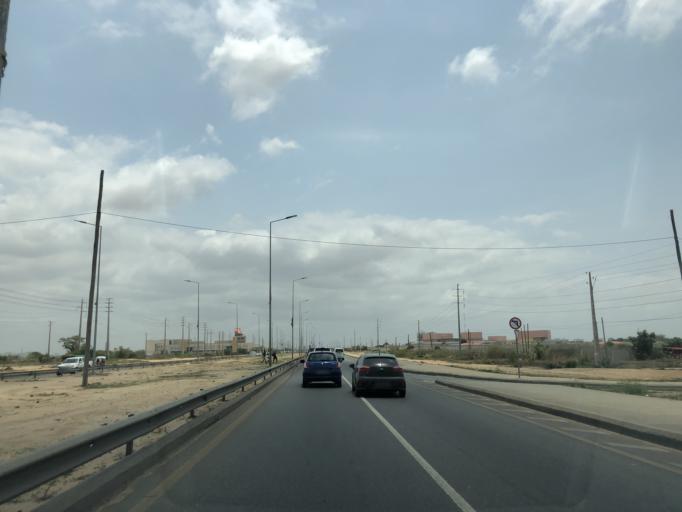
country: AO
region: Luanda
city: Luanda
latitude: -8.9541
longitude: 13.2583
